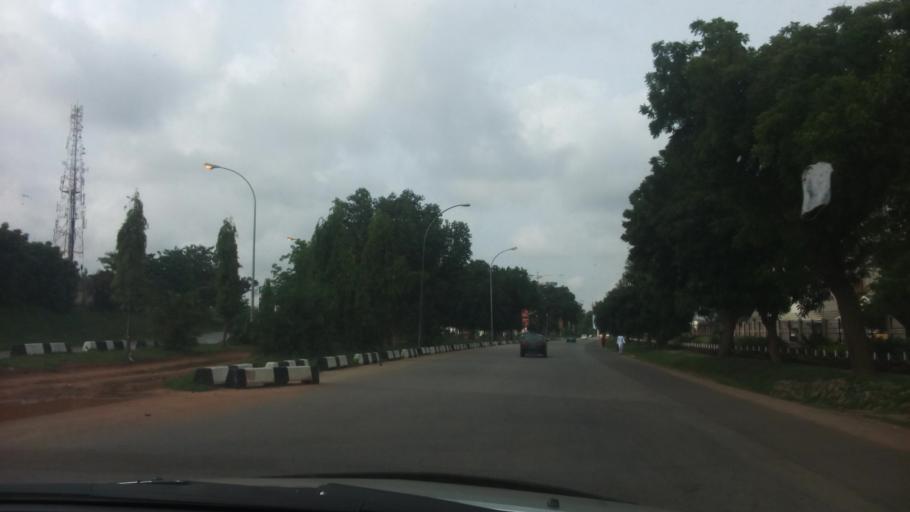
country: NG
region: Abuja Federal Capital Territory
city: Abuja
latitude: 9.0757
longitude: 7.4965
